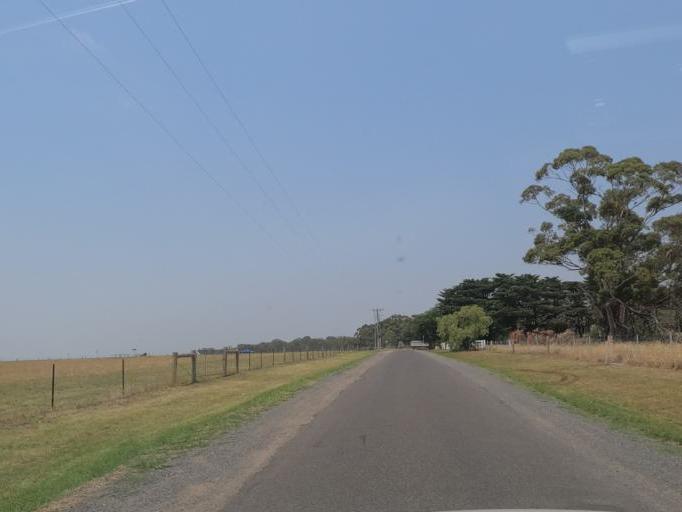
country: AU
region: Victoria
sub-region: Hume
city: Greenvale
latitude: -37.6415
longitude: 144.8292
